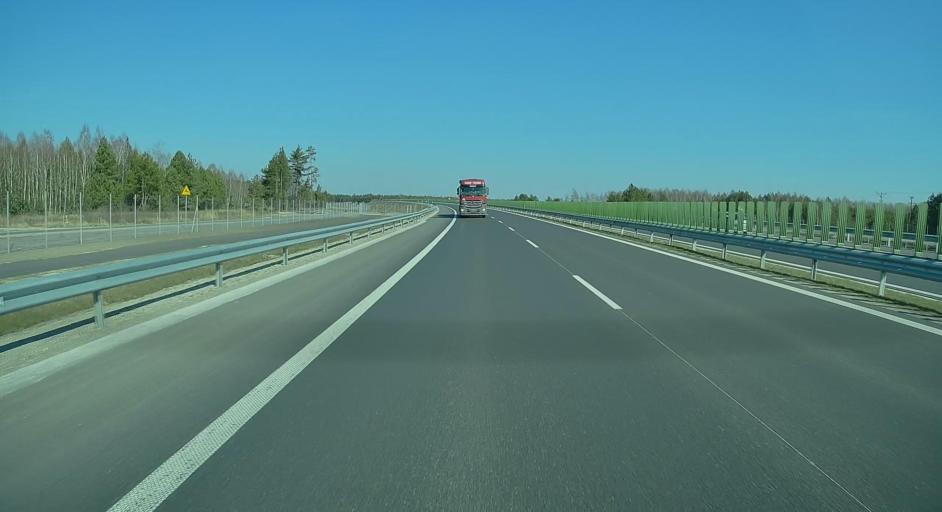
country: PL
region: Subcarpathian Voivodeship
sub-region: Powiat nizanski
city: Konczyce
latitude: 50.4346
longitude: 22.1370
